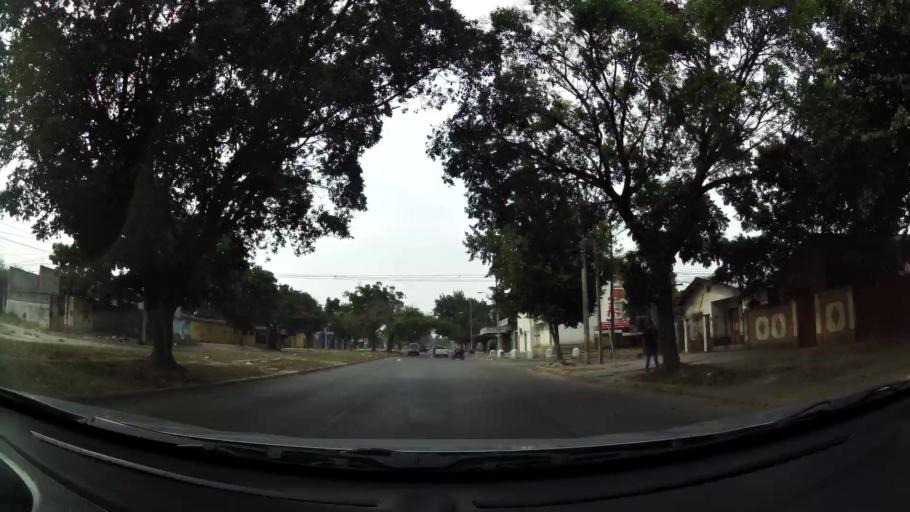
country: HN
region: Cortes
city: San Pedro Sula
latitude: 15.4951
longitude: -88.0156
